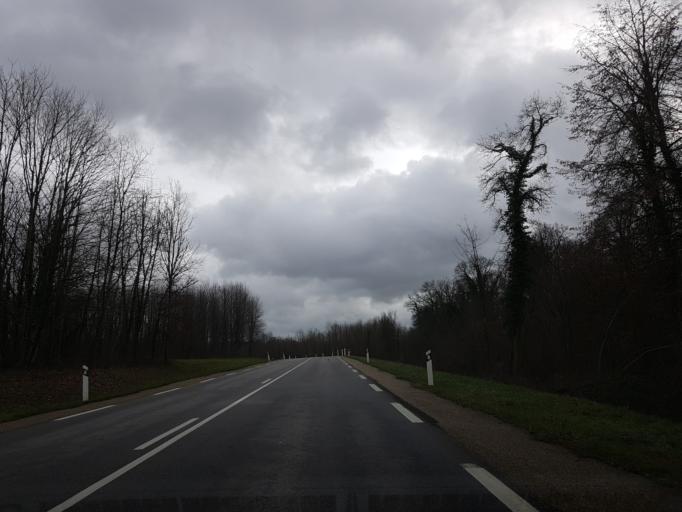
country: FR
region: Champagne-Ardenne
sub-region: Departement de la Haute-Marne
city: Fayl-Billot
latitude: 47.7977
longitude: 5.5630
